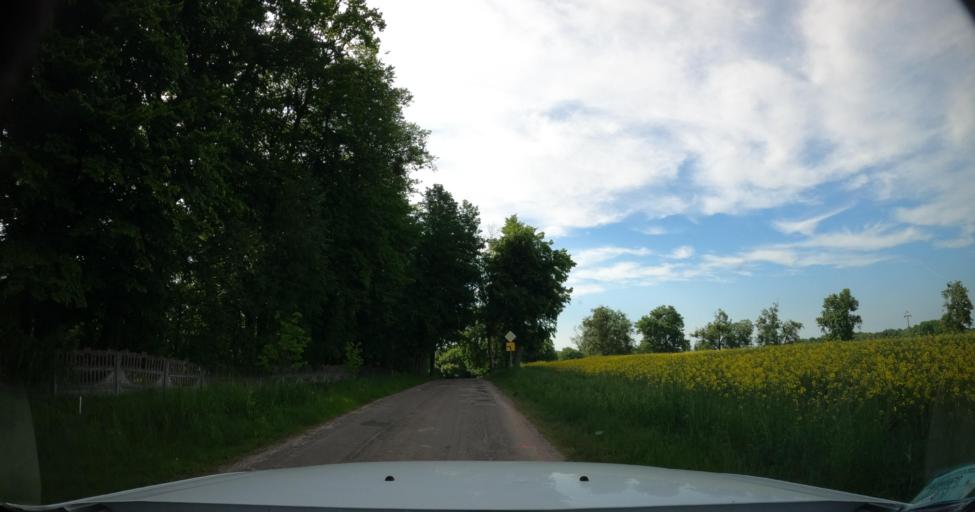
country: PL
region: Warmian-Masurian Voivodeship
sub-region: Powiat ostrodzki
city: Morag
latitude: 54.0195
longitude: 19.9159
